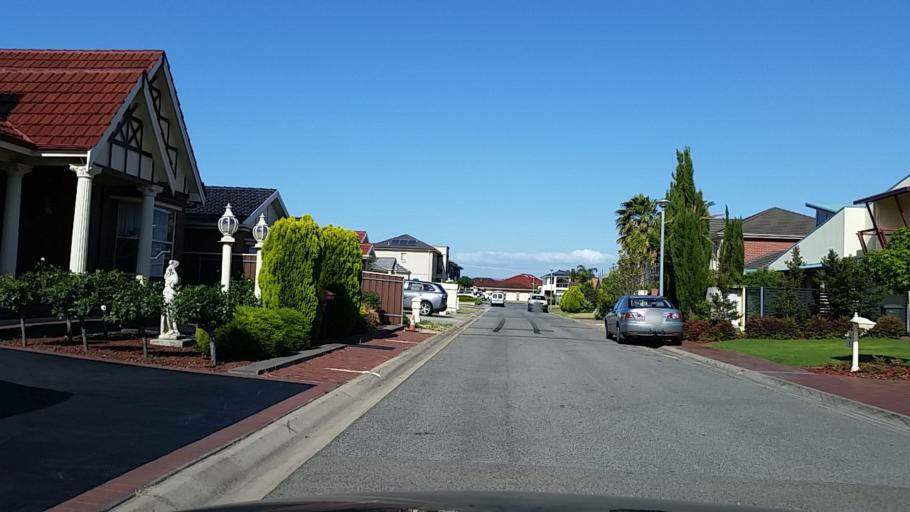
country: AU
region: South Australia
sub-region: Charles Sturt
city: Henley Beach
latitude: -34.9155
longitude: 138.5064
